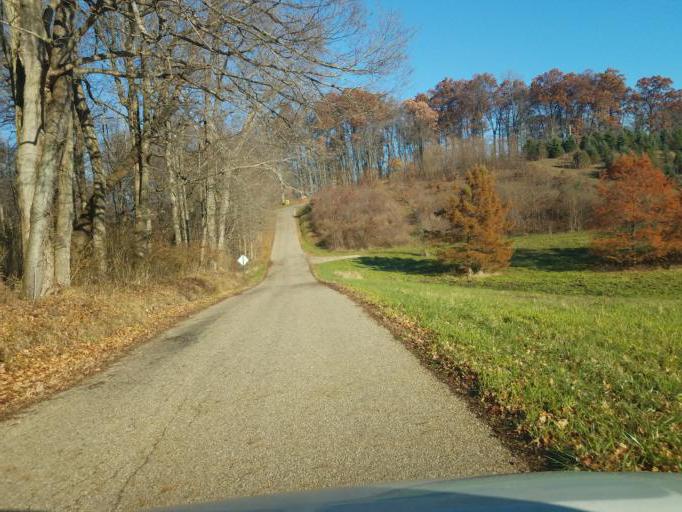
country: US
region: Ohio
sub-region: Sandusky County
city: Bellville
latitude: 40.6584
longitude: -82.5015
